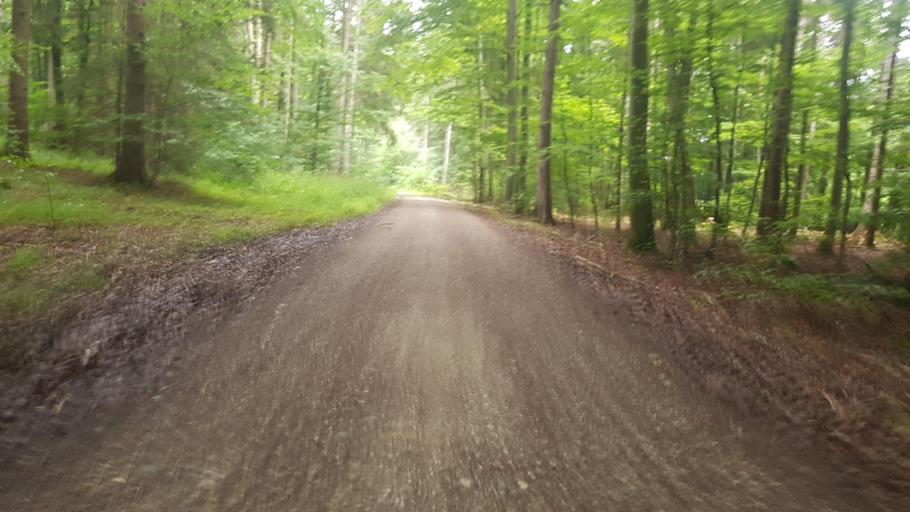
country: DE
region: Bavaria
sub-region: Upper Bavaria
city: Gauting
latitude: 48.0374
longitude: 11.3573
